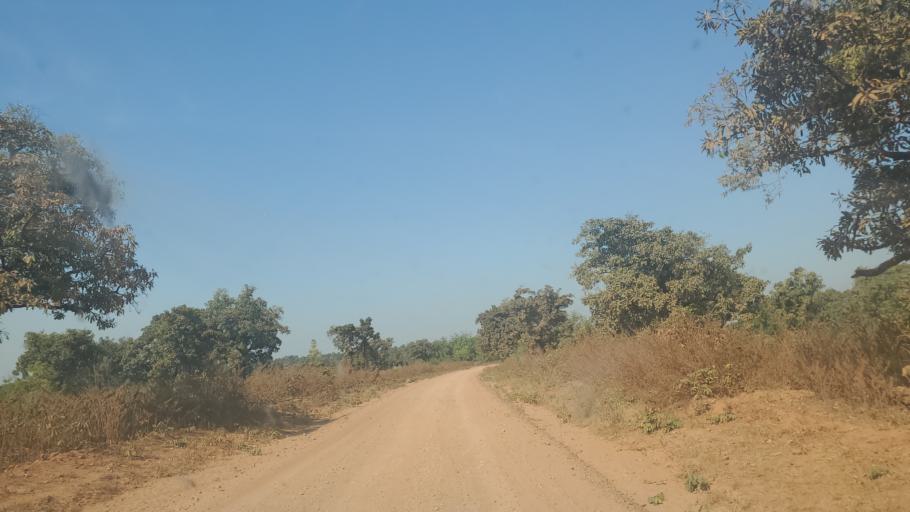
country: NG
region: Niger
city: Badeggi
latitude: 9.1238
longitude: 6.1932
